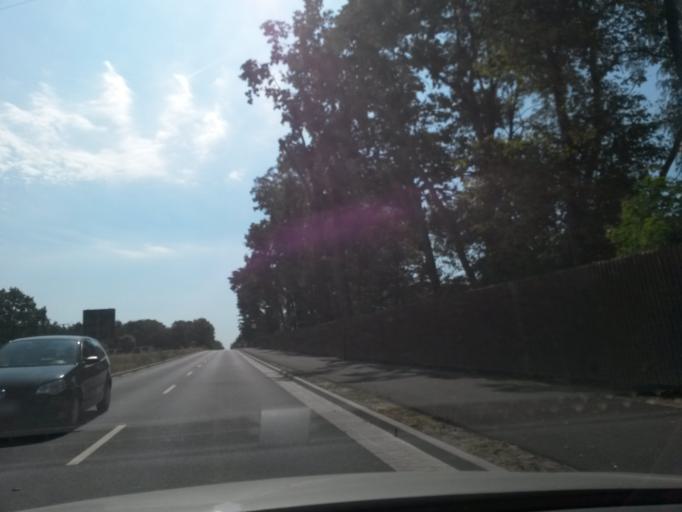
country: DE
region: Saxony-Anhalt
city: Jerichow
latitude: 52.4340
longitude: 11.9974
